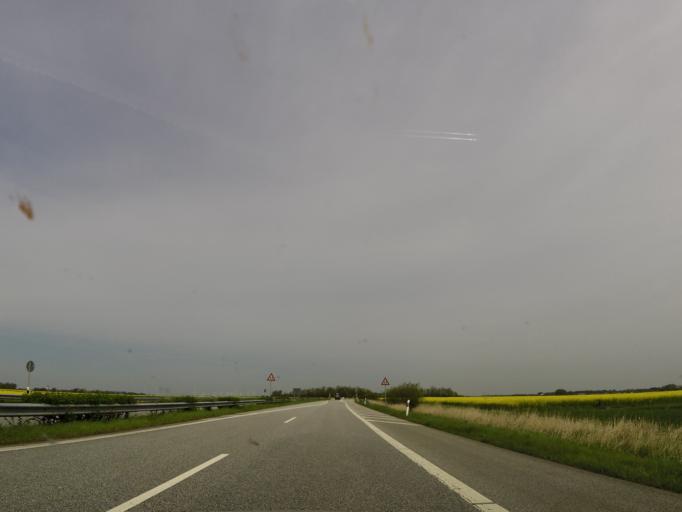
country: DE
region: Schleswig-Holstein
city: Lohe-Rickelshof
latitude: 54.1944
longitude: 9.0452
